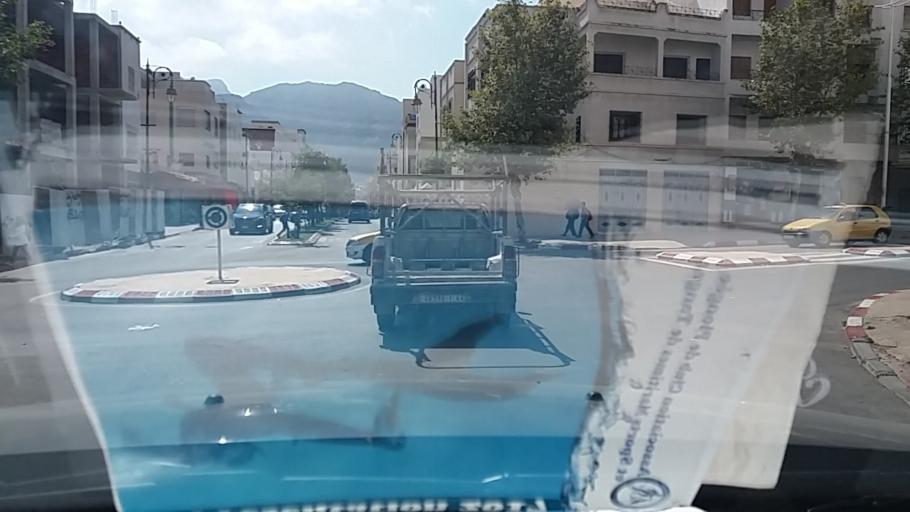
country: MA
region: Tanger-Tetouan
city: Tetouan
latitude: 35.5658
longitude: -5.3580
